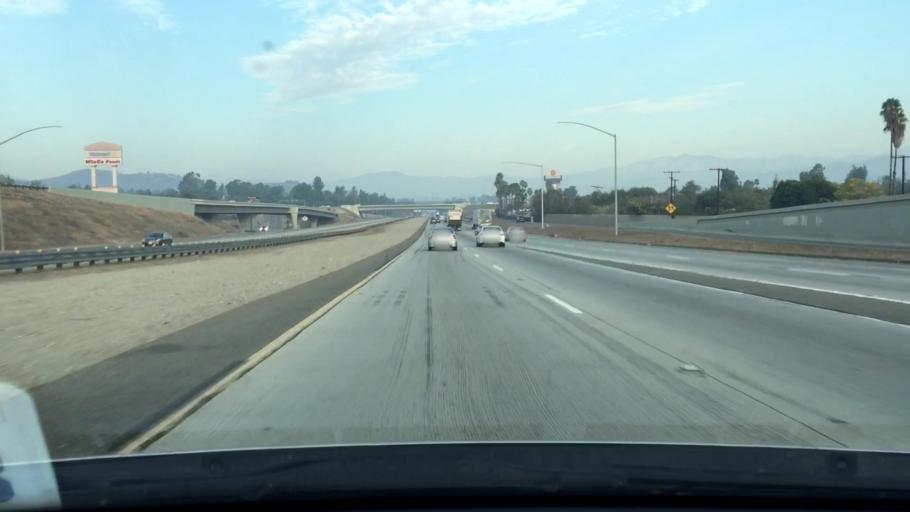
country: US
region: California
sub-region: Los Angeles County
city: Pomona
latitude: 34.0274
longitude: -117.7534
